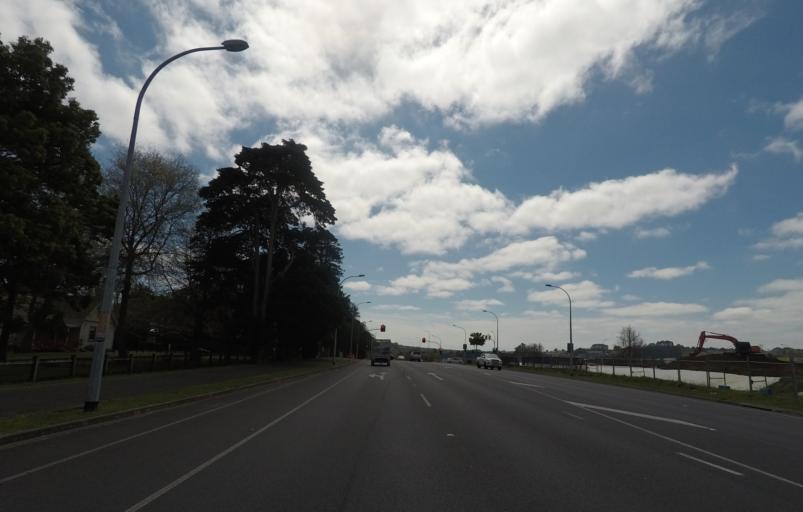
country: NZ
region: Auckland
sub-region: Auckland
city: Manukau City
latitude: -36.9760
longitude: 174.9223
